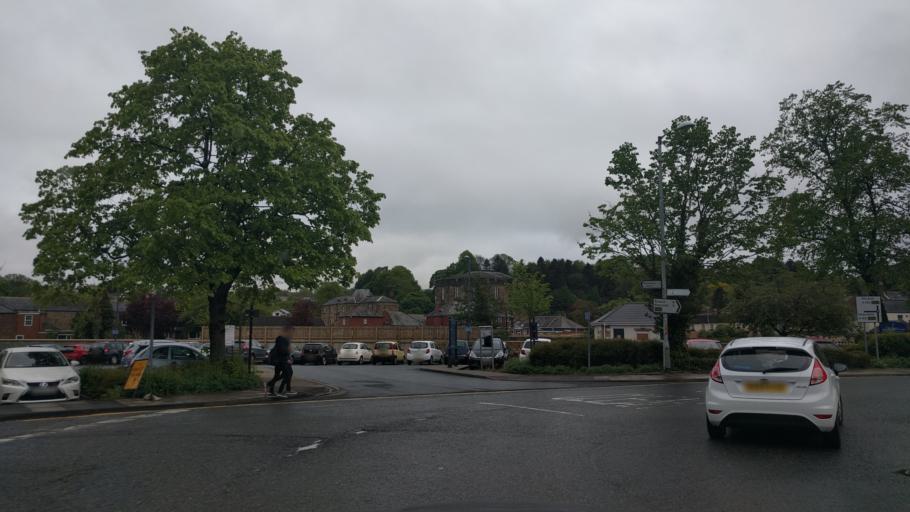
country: GB
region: England
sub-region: Northumberland
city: Morpeth
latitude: 55.1673
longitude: -1.6854
